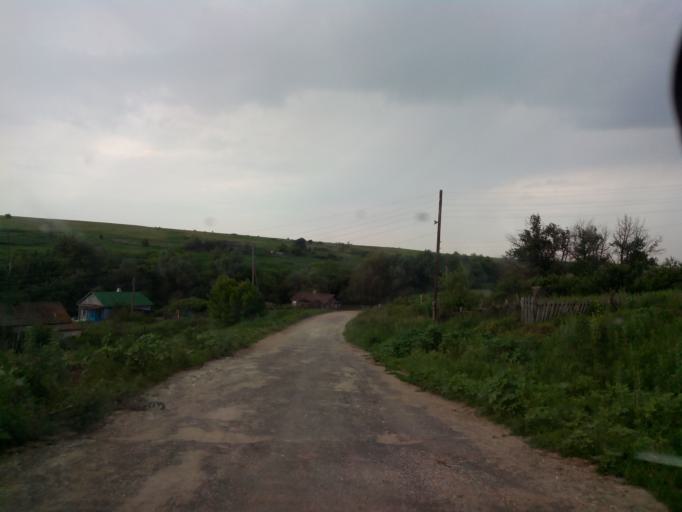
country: RU
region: Volgograd
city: Slashchevskaya
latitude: 49.7775
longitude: 42.4575
